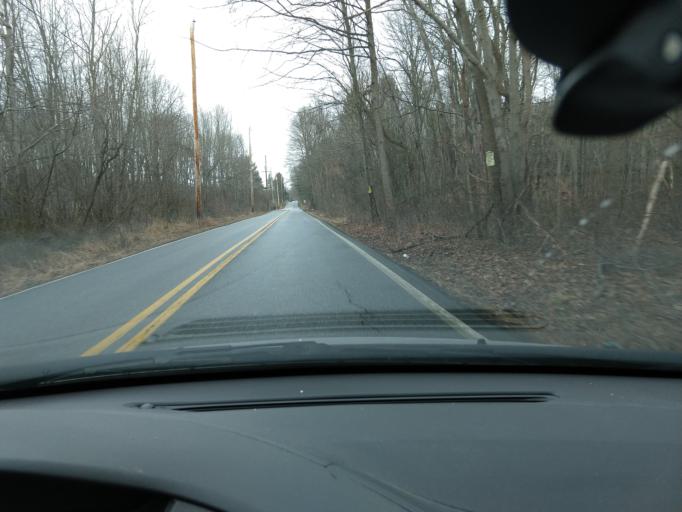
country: US
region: Pennsylvania
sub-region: Montgomery County
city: Stowe
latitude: 40.1928
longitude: -75.7071
